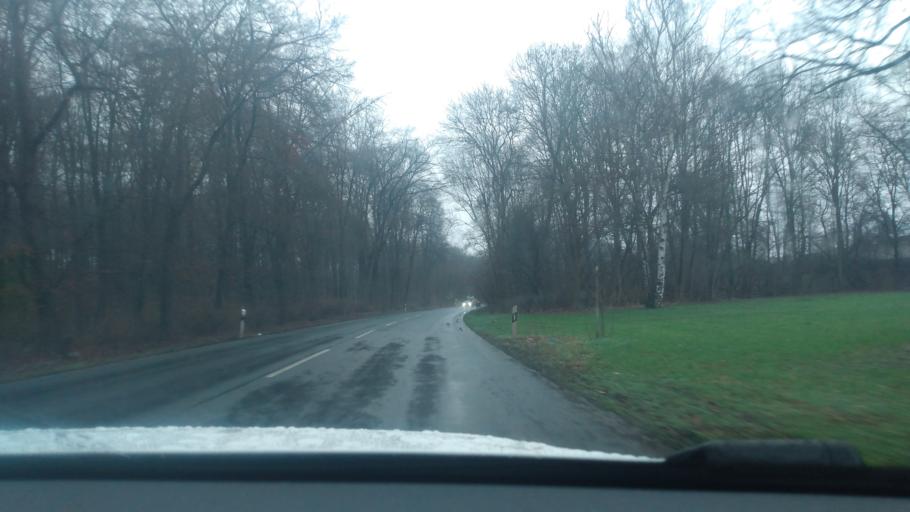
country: DE
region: North Rhine-Westphalia
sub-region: Regierungsbezirk Koln
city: Hurth
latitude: 50.9179
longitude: 6.8920
